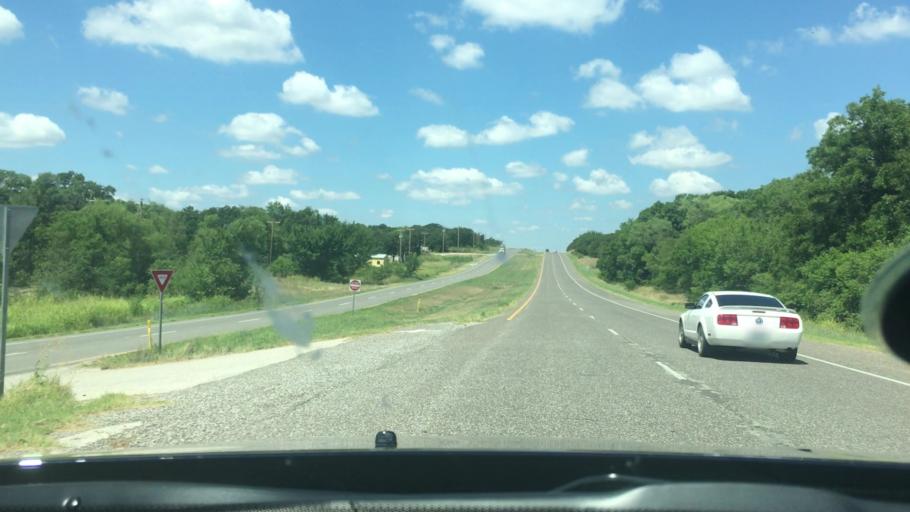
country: US
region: Oklahoma
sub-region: Carter County
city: Lone Grove
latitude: 34.1731
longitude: -97.2866
